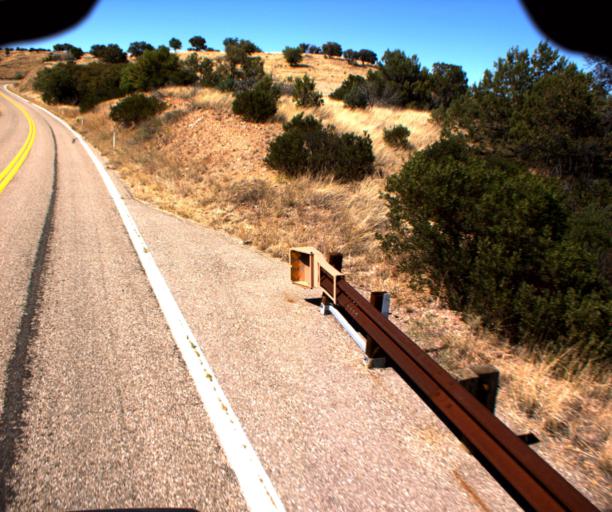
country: US
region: Arizona
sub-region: Cochise County
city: Sierra Vista
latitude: 31.4962
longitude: -110.4932
